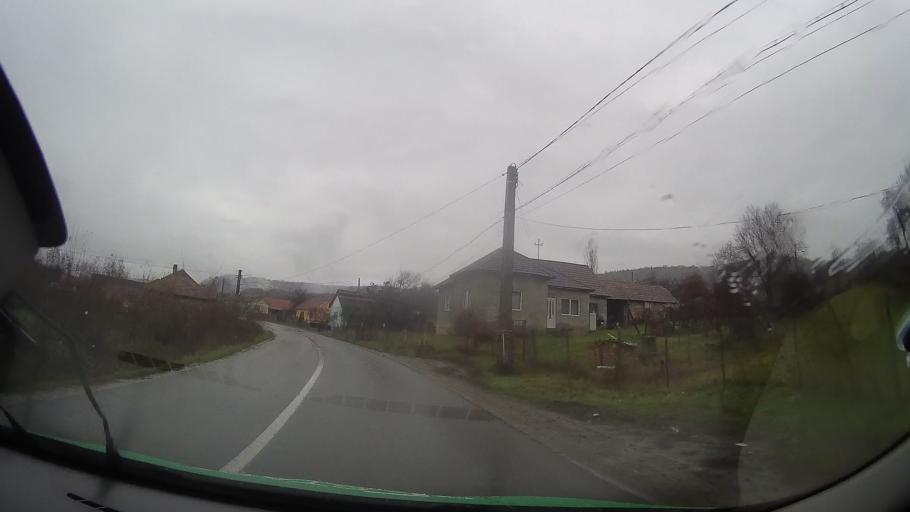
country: RO
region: Bistrita-Nasaud
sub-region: Comuna Mariselu
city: Mariselu
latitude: 47.0146
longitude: 24.5528
